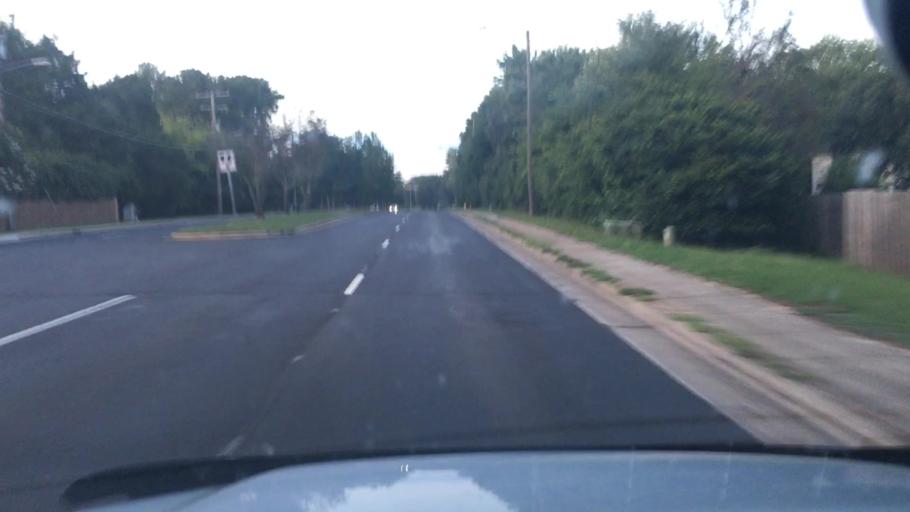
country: US
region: North Carolina
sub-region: Mecklenburg County
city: Pineville
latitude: 35.0955
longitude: -80.8408
